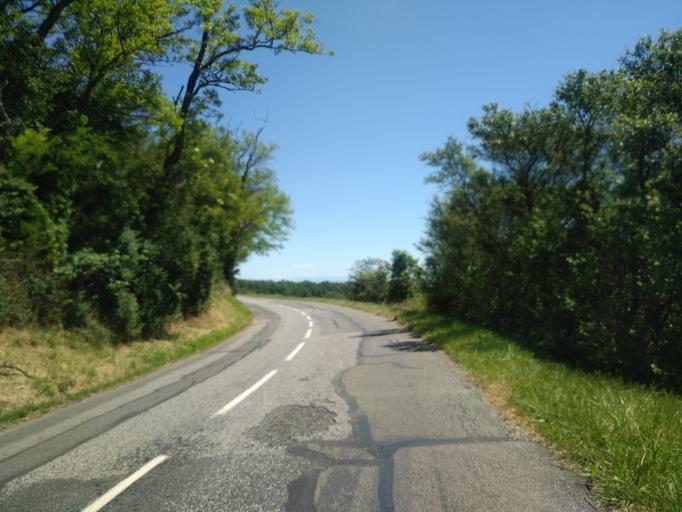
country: FR
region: Rhone-Alpes
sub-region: Departement du Rhone
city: Limonest
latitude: 45.8393
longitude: 4.7951
